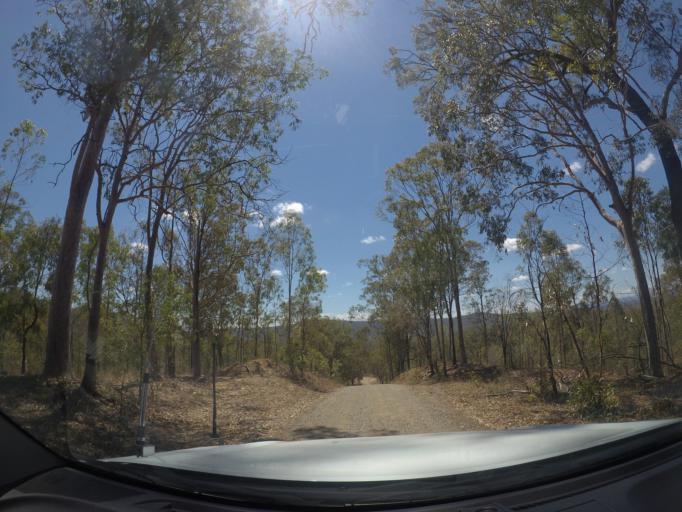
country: AU
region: Queensland
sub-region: Ipswich
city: Deebing Heights
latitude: -27.8281
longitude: 152.8348
